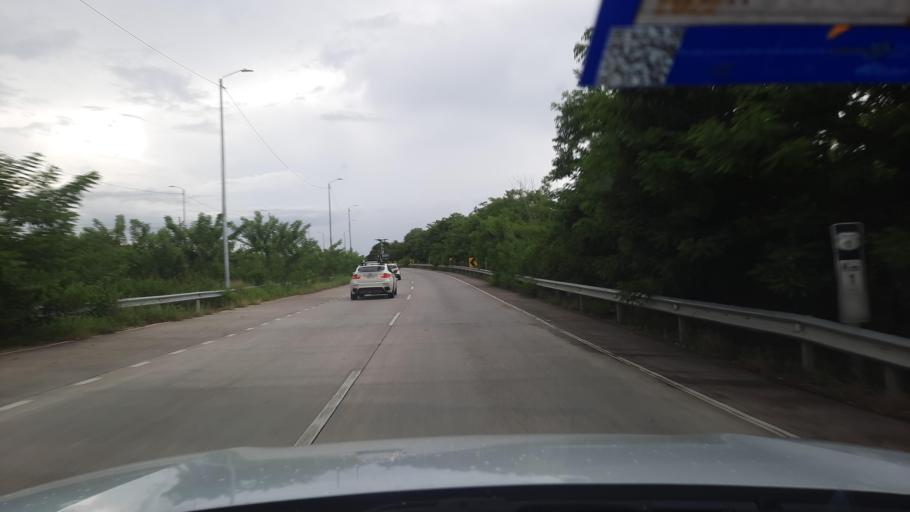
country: CR
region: Guanacaste
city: Bagaces
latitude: 10.5318
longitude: -85.2731
